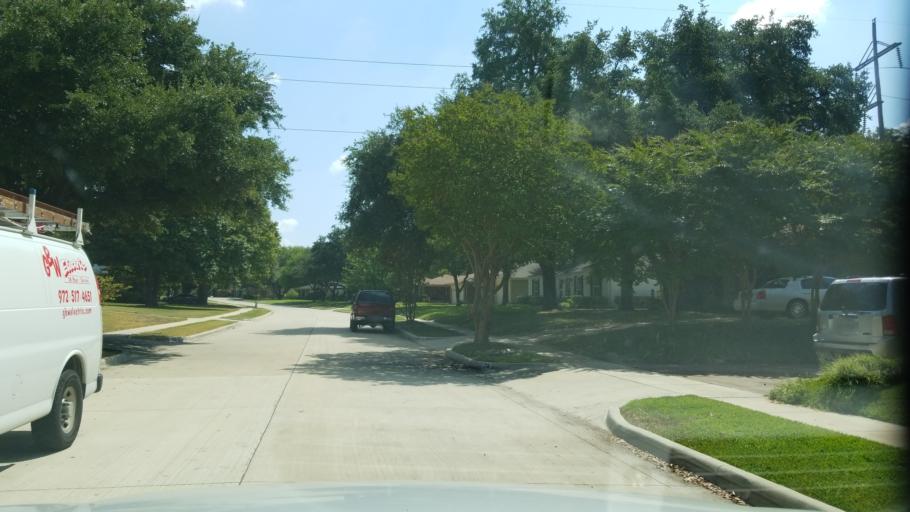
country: US
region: Texas
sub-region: Dallas County
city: Richardson
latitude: 32.9568
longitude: -96.7458
